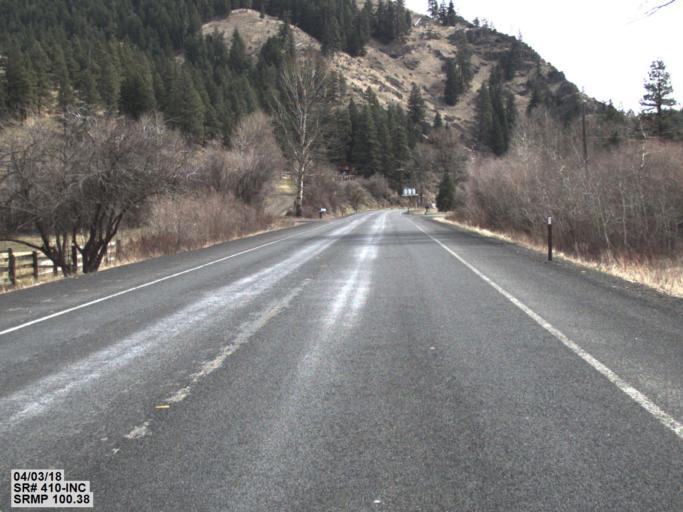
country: US
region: Washington
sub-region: Kittitas County
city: Cle Elum
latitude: 46.8984
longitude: -121.0081
